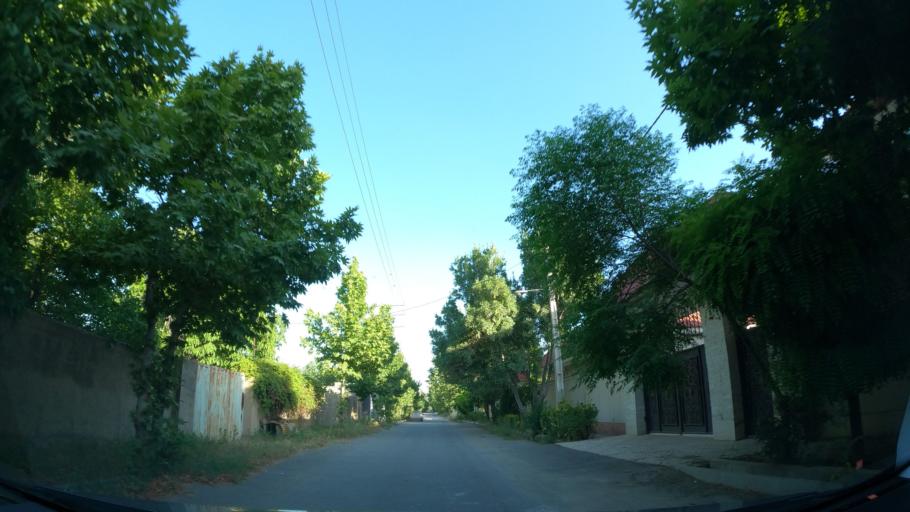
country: IR
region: Alborz
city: Hashtgerd
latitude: 35.9123
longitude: 50.7201
